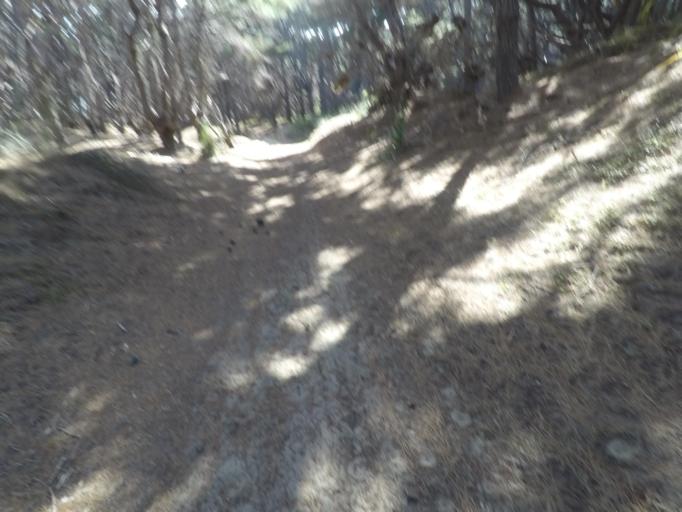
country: NZ
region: Auckland
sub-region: Auckland
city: Parakai
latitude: -36.6055
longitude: 174.2716
